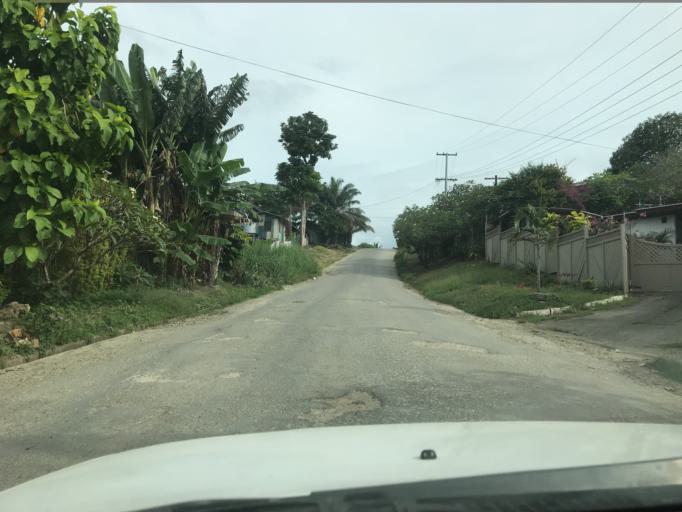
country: SB
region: Guadalcanal
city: Honiara
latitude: -9.4353
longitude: 159.9452
